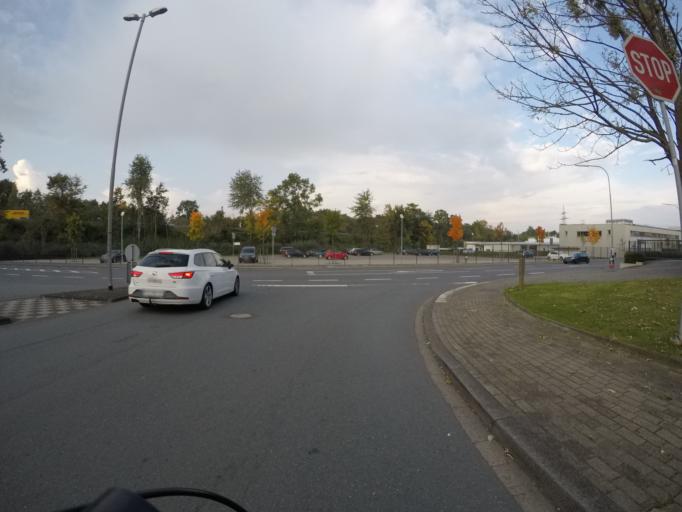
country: DE
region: North Rhine-Westphalia
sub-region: Regierungsbezirk Detmold
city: Herford
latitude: 52.1308
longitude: 8.6514
